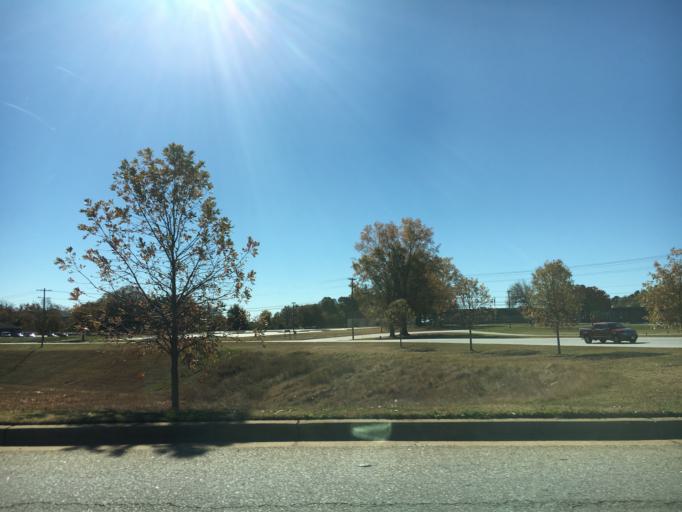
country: US
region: South Carolina
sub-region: Spartanburg County
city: Roebuck
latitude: 34.8380
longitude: -81.9963
